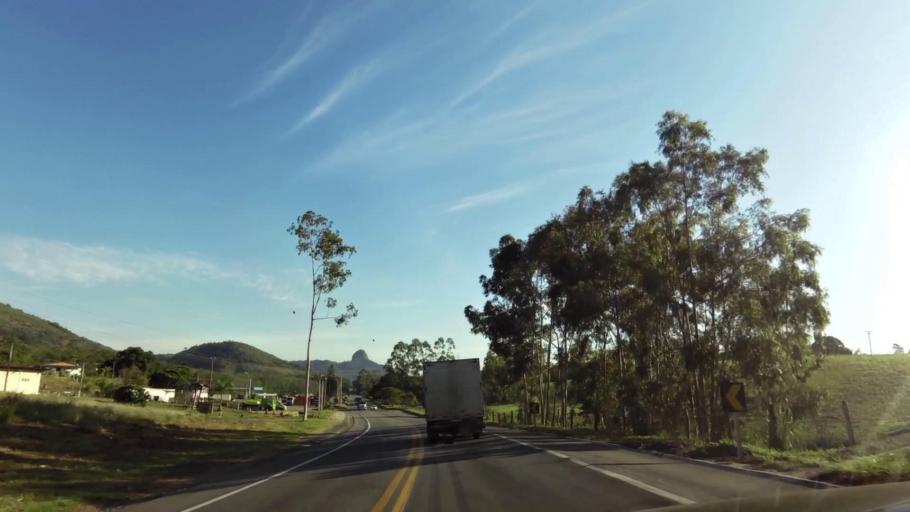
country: BR
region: Espirito Santo
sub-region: Guarapari
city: Guarapari
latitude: -20.5596
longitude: -40.4803
